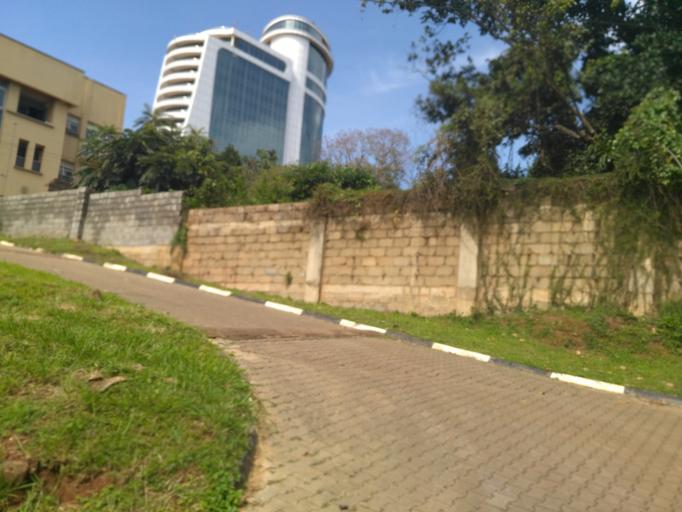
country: UG
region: Central Region
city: Kampala Central Division
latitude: 0.3240
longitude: 32.5800
